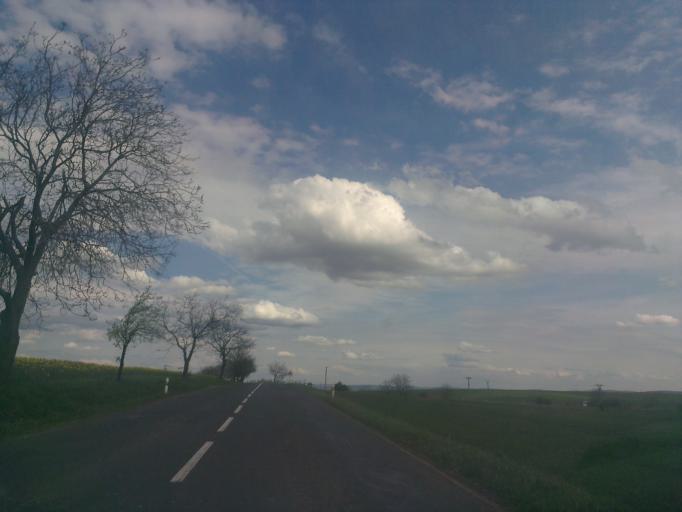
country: CZ
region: South Moravian
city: Orechov
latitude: 49.1104
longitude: 16.5368
